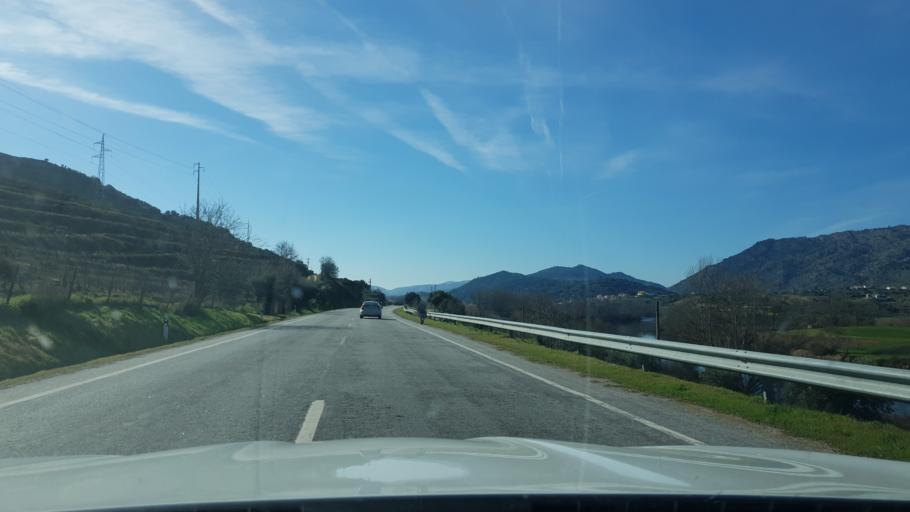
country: PT
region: Braganca
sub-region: Torre de Moncorvo
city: Torre de Moncorvo
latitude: 41.1943
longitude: -7.0973
